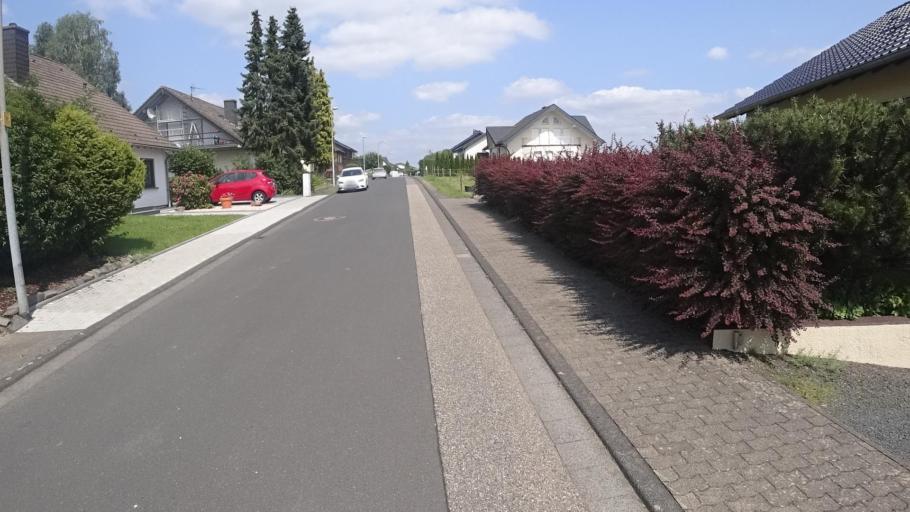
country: DE
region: Rheinland-Pfalz
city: Vettelschoss
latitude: 50.5948
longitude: 7.3475
